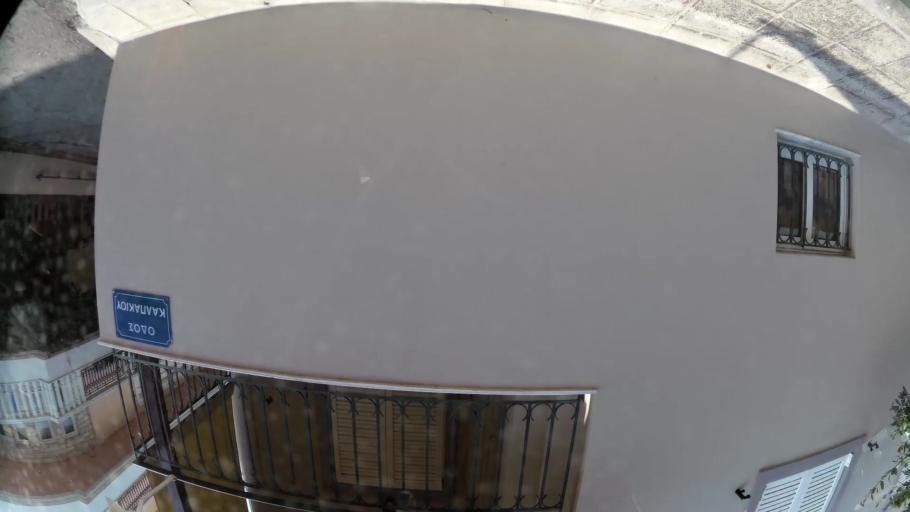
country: GR
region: Attica
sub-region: Nomarchia Dytikis Attikis
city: Zefyri
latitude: 38.0646
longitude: 23.7165
